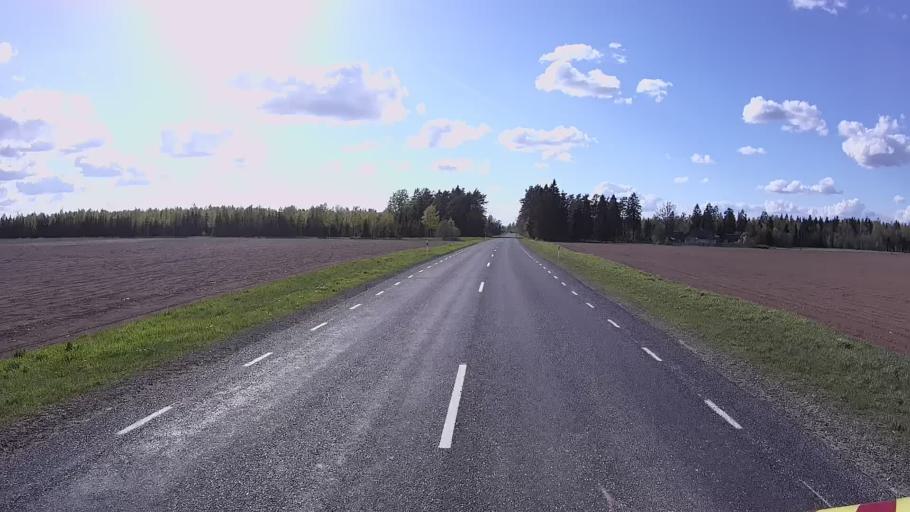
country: EE
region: Jogevamaa
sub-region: Jogeva linn
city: Jogeva
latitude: 58.7376
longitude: 26.2697
